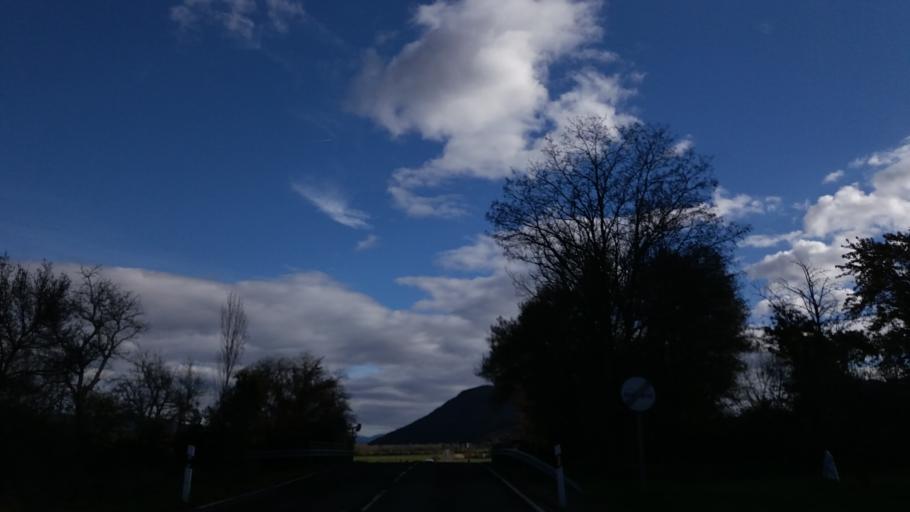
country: ES
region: Aragon
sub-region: Provincia de Huesca
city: Santa Cruz de la Seros
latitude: 42.5570
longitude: -0.7029
